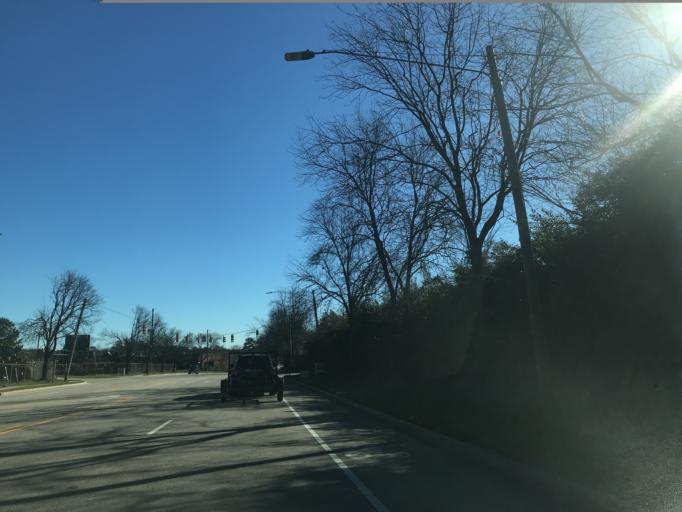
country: US
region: North Carolina
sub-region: Wake County
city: West Raleigh
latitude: 35.7930
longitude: -78.7055
